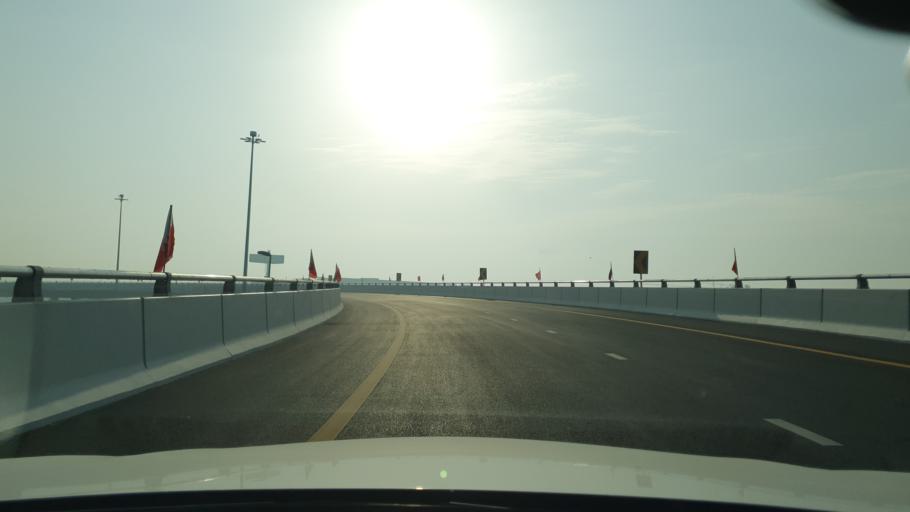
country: BH
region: Northern
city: Madinat `Isa
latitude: 26.1827
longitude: 50.5005
